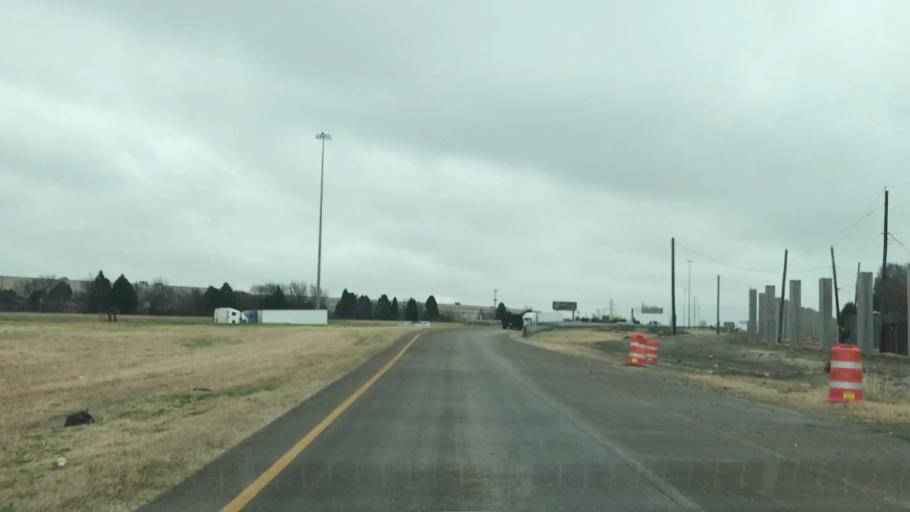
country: US
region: Texas
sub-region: Dallas County
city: Richardson
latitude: 32.8929
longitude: -96.7118
